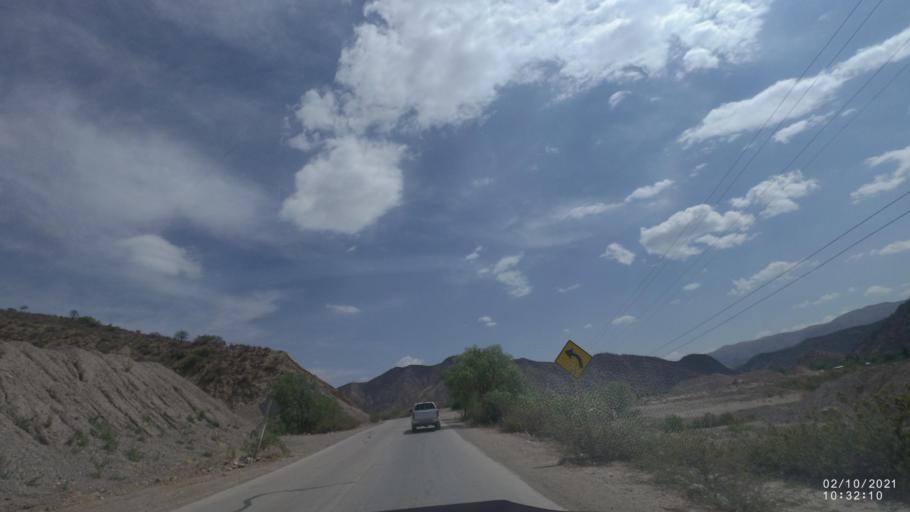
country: BO
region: Cochabamba
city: Capinota
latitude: -17.6908
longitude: -66.2574
